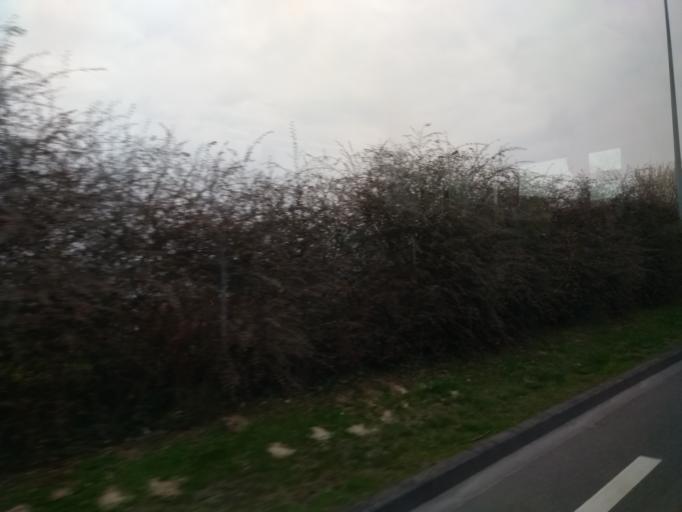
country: FR
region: Picardie
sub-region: Departement de l'Oise
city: Jaux
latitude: 49.3886
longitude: 2.7939
